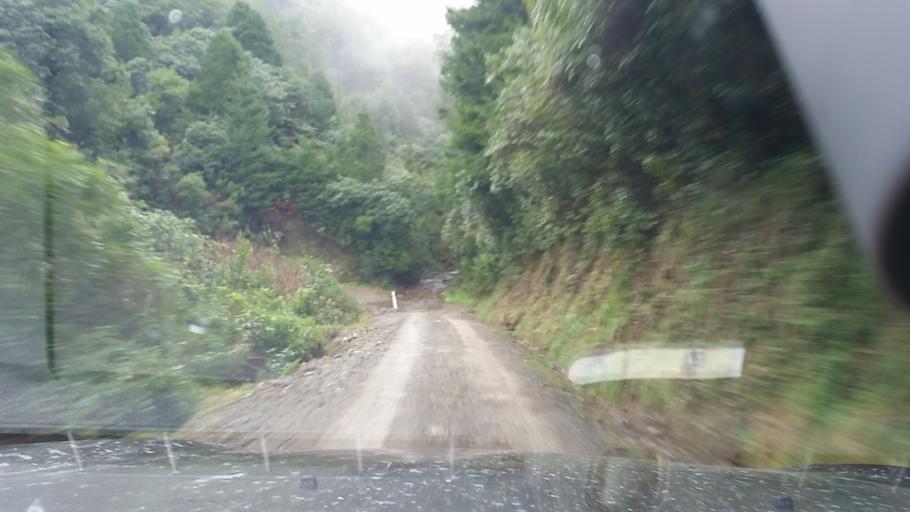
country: NZ
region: Nelson
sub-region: Nelson City
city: Nelson
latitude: -41.3711
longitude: 173.6091
